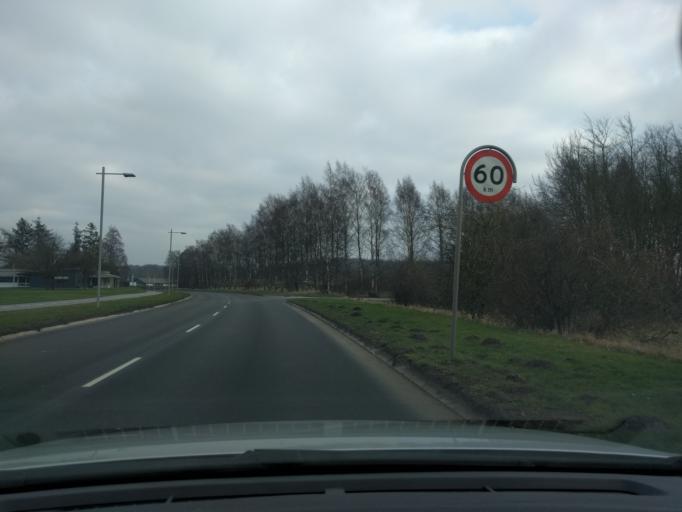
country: DK
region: Zealand
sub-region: Guldborgsund Kommune
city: Nykobing Falster
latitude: 54.7487
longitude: 11.8852
